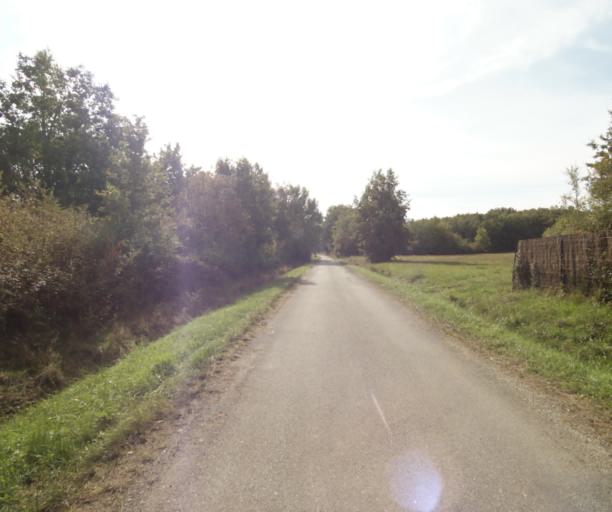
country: FR
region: Midi-Pyrenees
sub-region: Departement du Tarn-et-Garonne
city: Orgueil
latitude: 43.8896
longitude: 1.4030
